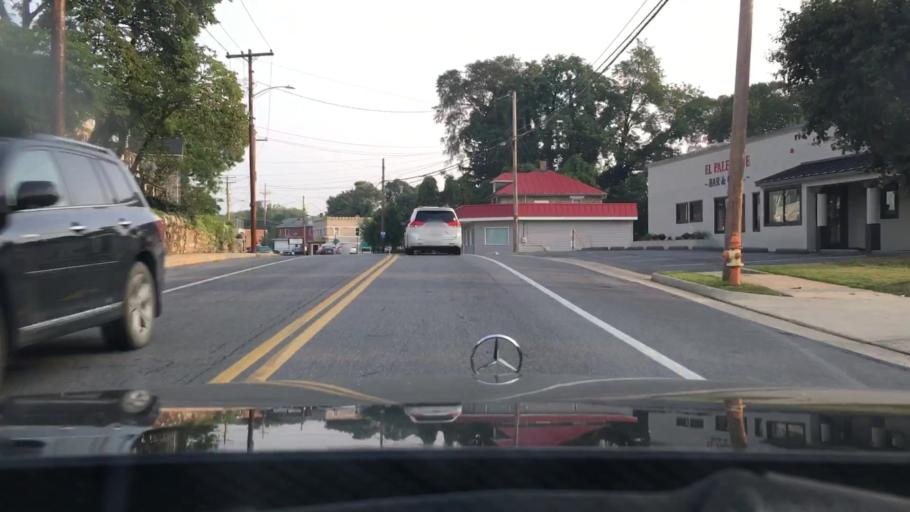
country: US
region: Virginia
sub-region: City of Winchester
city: Winchester
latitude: 39.1735
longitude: -78.1650
